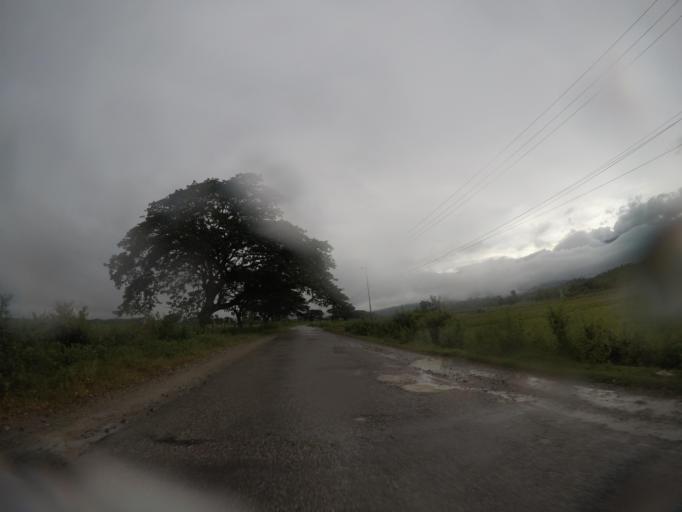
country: TL
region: Bobonaro
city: Maliana
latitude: -8.9910
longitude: 125.1811
